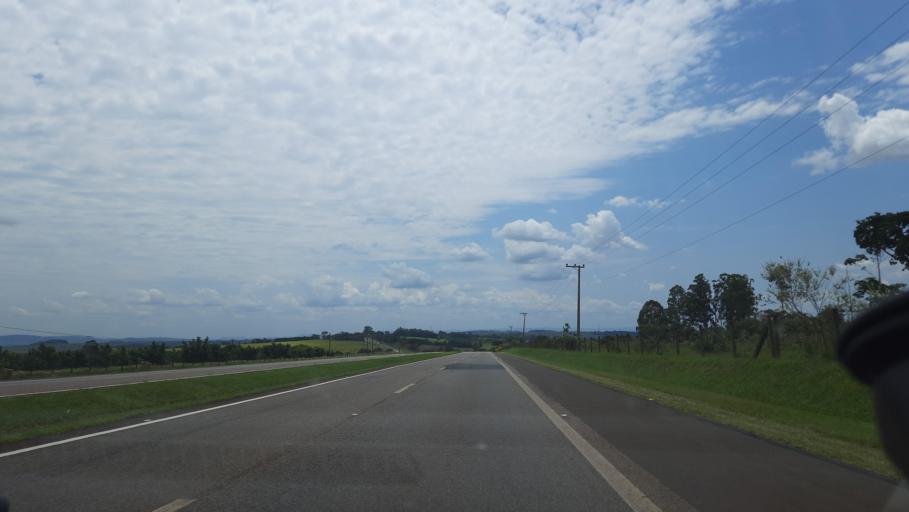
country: BR
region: Sao Paulo
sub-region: Casa Branca
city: Casa Branca
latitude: -21.7403
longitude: -47.0730
